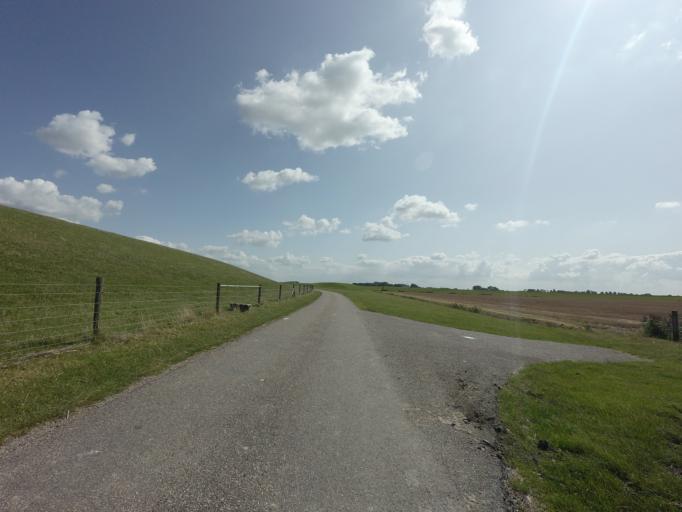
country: NL
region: Friesland
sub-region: Gemeente Ferwerderadiel
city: Hallum
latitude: 53.3197
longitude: 5.7519
